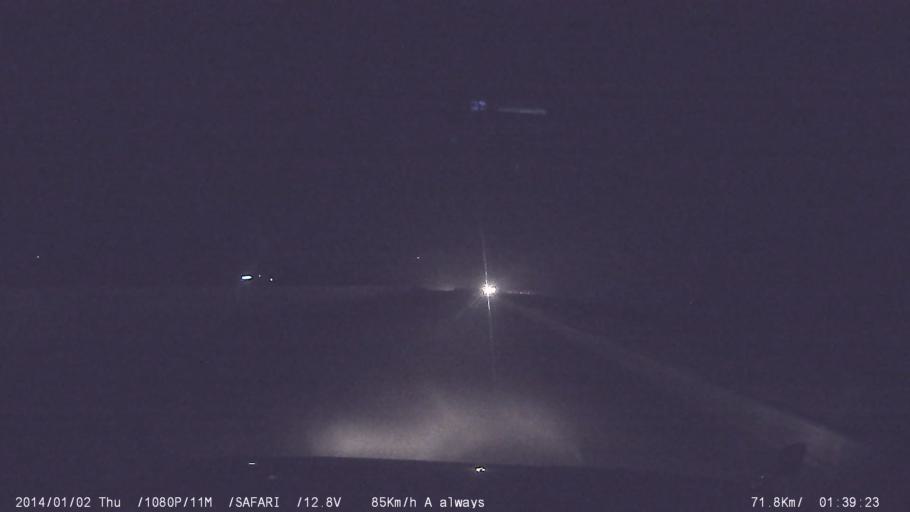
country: IN
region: Tamil Nadu
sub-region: Tiruppur
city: Avinashi
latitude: 11.1436
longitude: 77.2049
